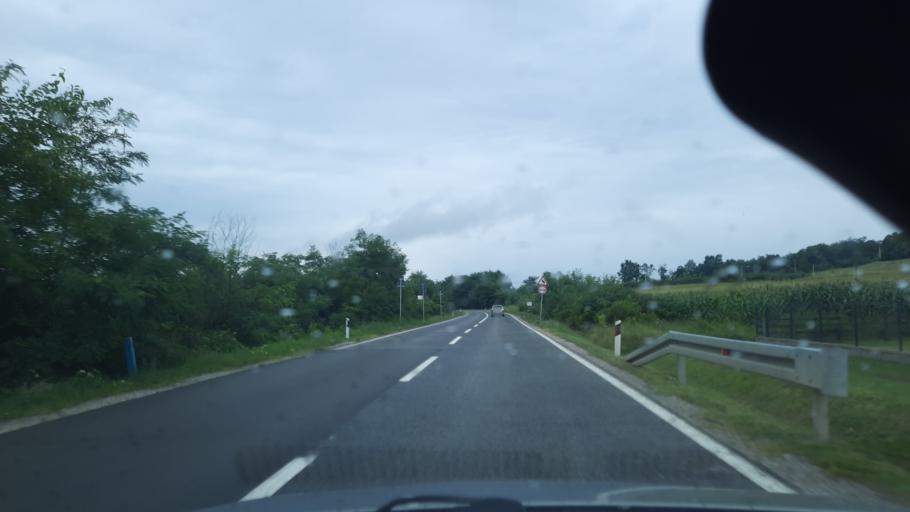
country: RS
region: Central Serbia
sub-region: Sumadijski Okrug
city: Knic
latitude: 43.8631
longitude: 20.7767
